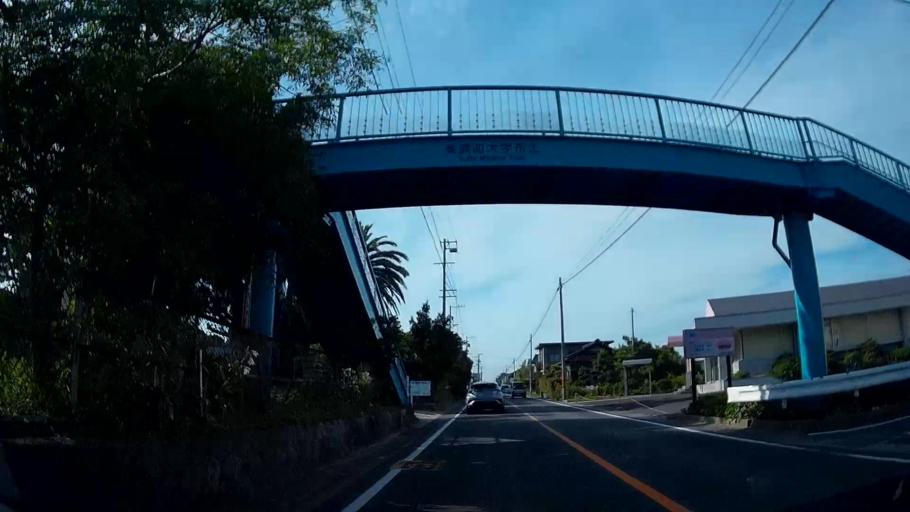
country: JP
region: Aichi
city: Taketoyo
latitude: 34.8000
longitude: 136.9188
